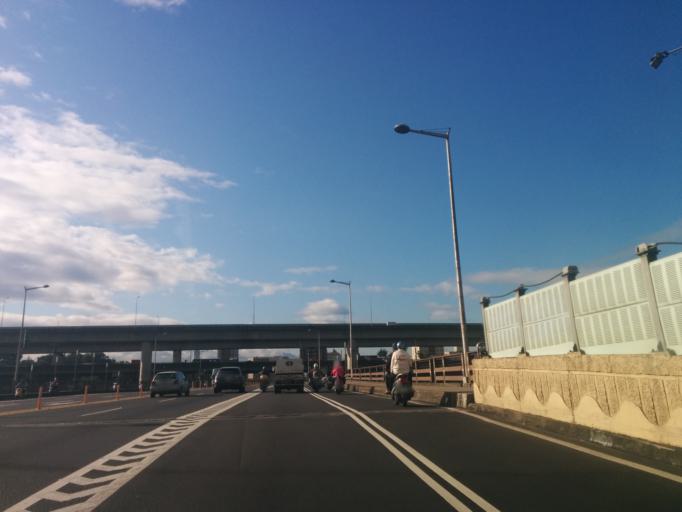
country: TW
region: Taipei
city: Taipei
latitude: 25.0791
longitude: 121.5215
